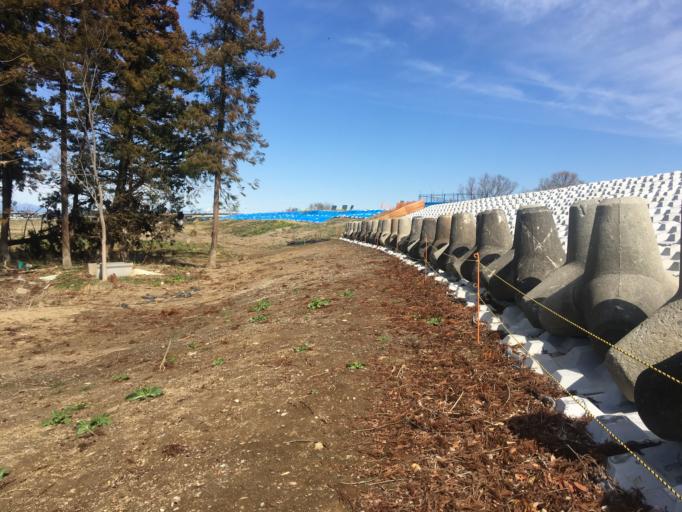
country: JP
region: Saitama
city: Sakado
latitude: 35.9984
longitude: 139.4224
